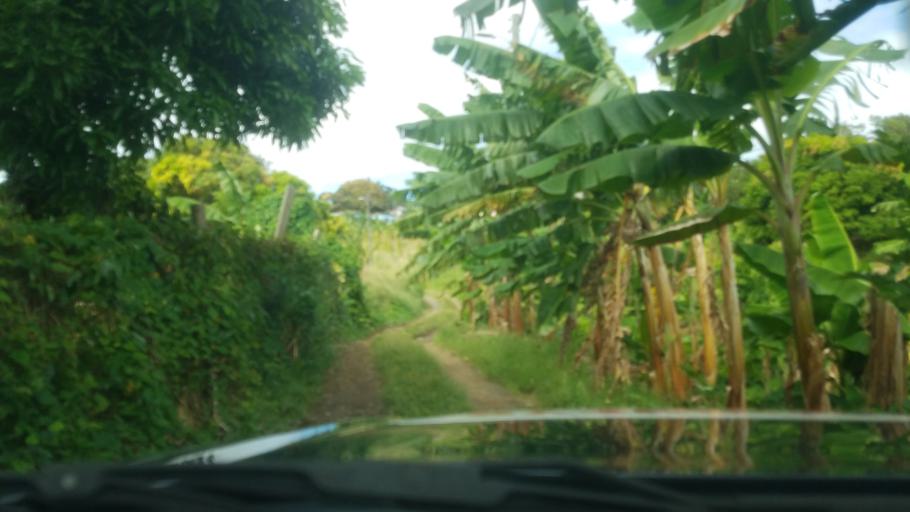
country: LC
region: Dennery Quarter
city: Dennery
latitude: 13.9331
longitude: -60.9230
